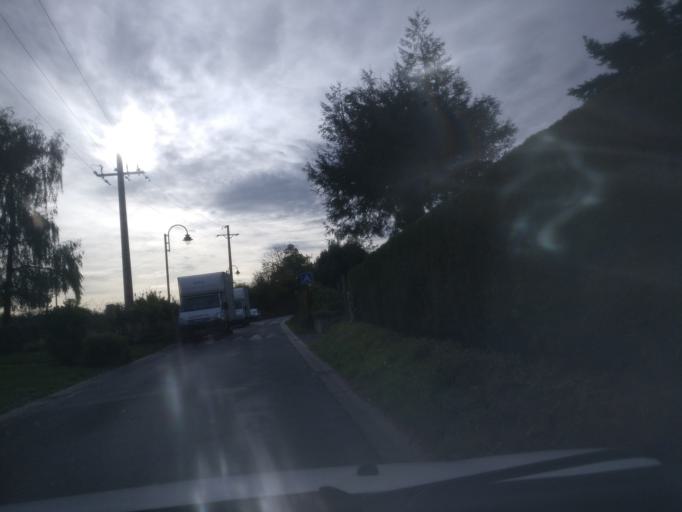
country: FR
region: Lower Normandy
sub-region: Departement de la Manche
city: Jullouville
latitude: 48.7489
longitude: -1.5556
